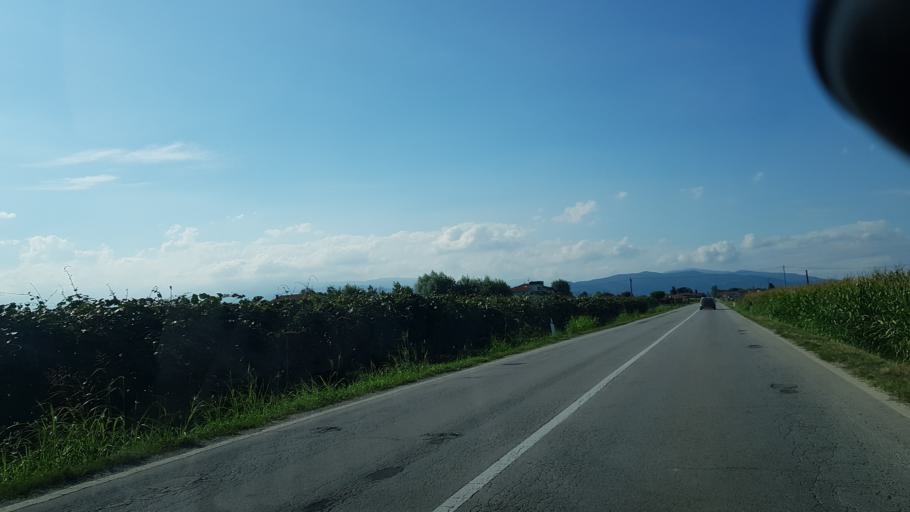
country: IT
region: Piedmont
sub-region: Provincia di Cuneo
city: Roata Rossi
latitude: 44.4309
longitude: 7.5387
